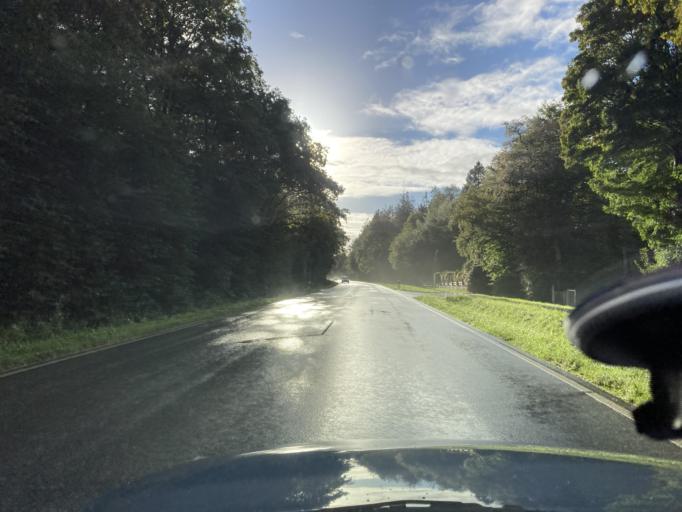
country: DE
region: Schleswig-Holstein
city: Welmbuttel
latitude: 54.2048
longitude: 9.2583
